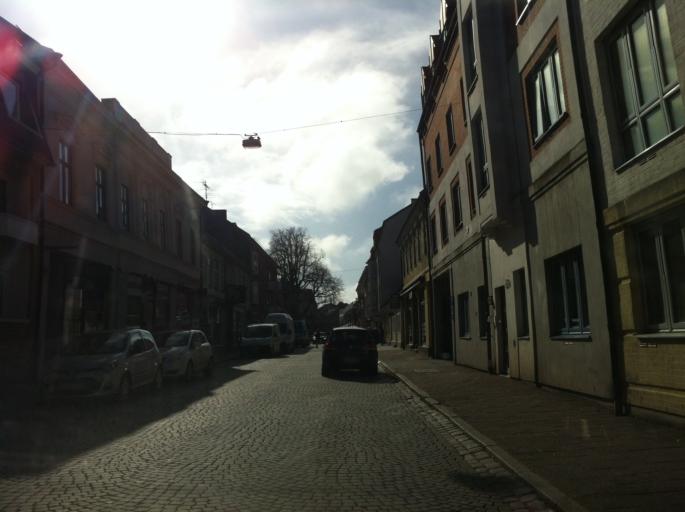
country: SE
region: Skane
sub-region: Angelholms Kommun
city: AEngelholm
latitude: 56.2474
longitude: 12.8653
